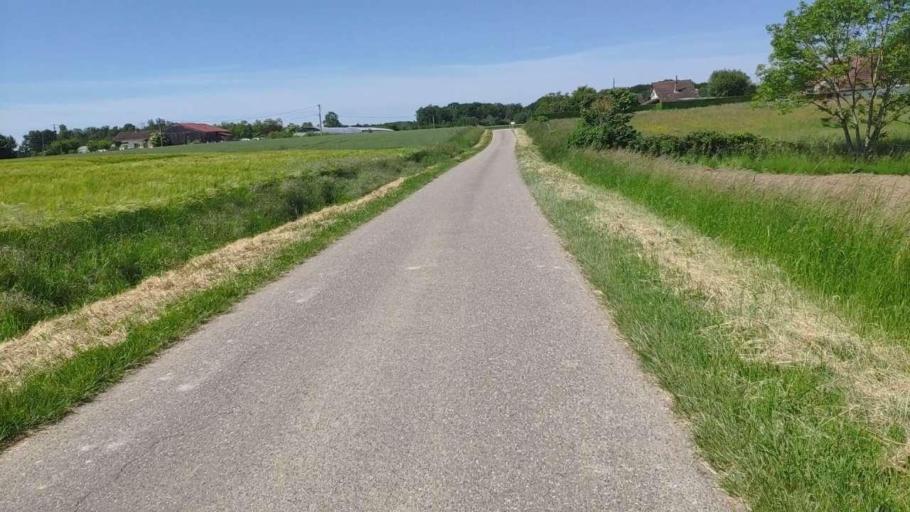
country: FR
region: Franche-Comte
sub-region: Departement du Jura
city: Bletterans
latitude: 46.7695
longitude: 5.4101
